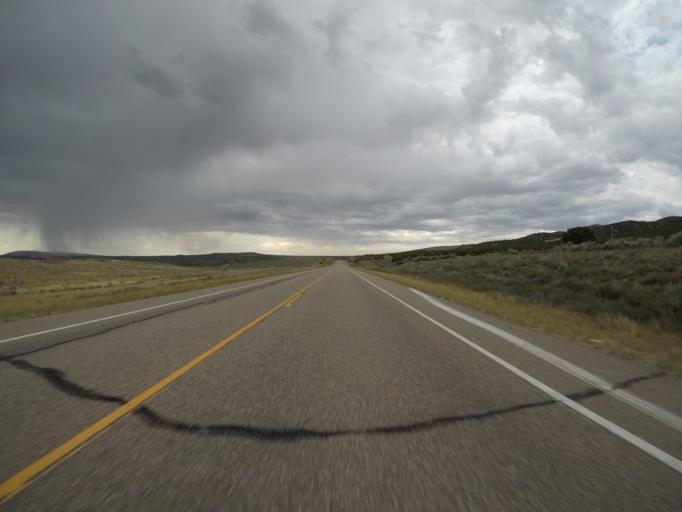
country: US
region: Colorado
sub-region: Rio Blanco County
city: Rangely
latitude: 40.3614
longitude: -108.4280
